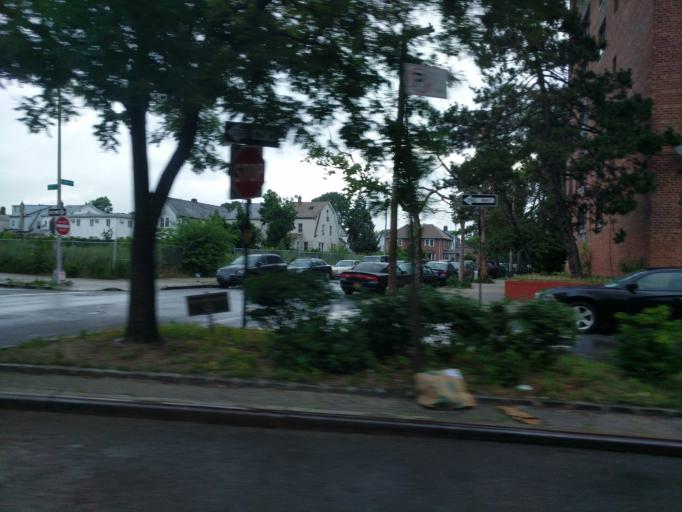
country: US
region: New York
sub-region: Queens County
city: Jamaica
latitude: 40.6972
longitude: -73.7841
